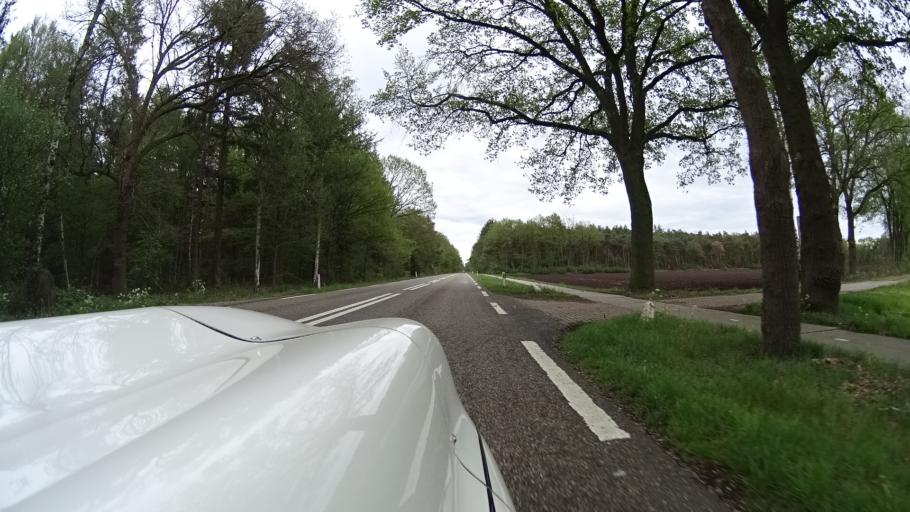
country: NL
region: North Brabant
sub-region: Gemeente Boxmeer
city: Overloon
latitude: 51.5405
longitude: 5.9042
